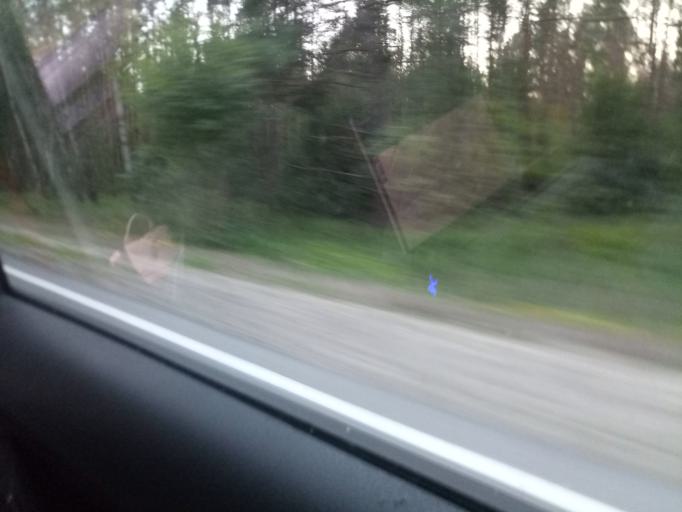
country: RU
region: Moskovskaya
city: Noginsk-9
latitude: 56.0943
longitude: 38.5815
